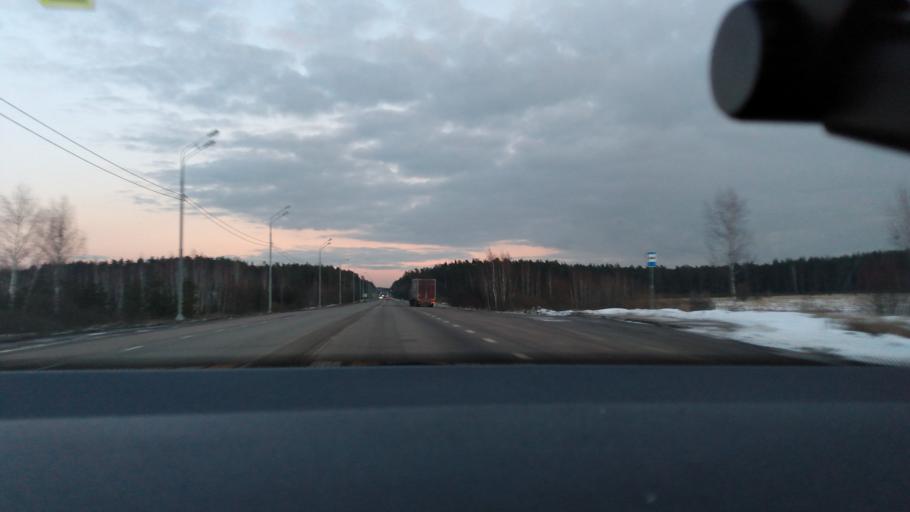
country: RU
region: Moskovskaya
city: Il'inskiy Pogost
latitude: 55.4889
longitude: 38.8795
